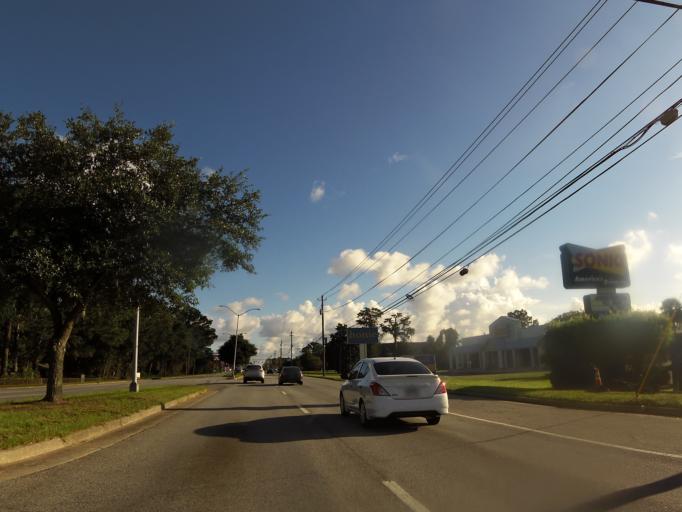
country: US
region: Georgia
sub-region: Glynn County
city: Country Club Estates
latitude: 31.1980
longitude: -81.4848
